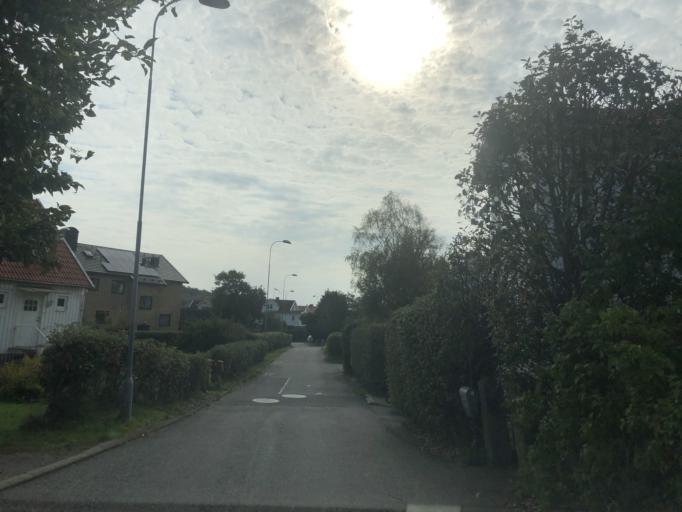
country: SE
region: Vaestra Goetaland
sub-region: Goteborg
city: Majorna
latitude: 57.6483
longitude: 11.8633
